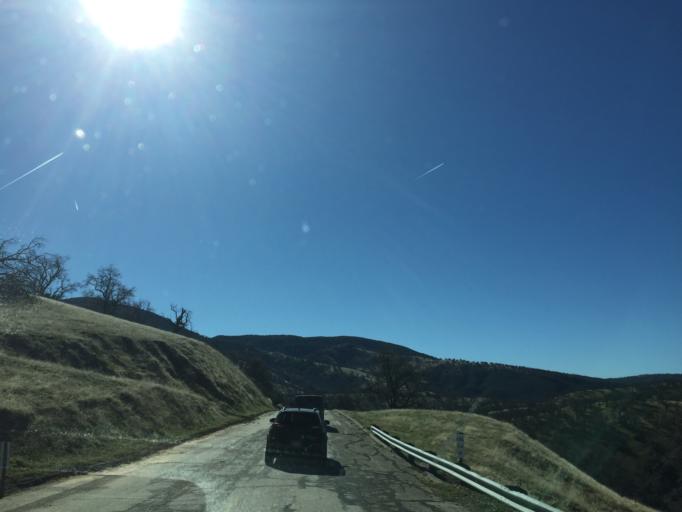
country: US
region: California
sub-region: Kern County
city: Lebec
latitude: 34.8922
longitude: -118.7850
